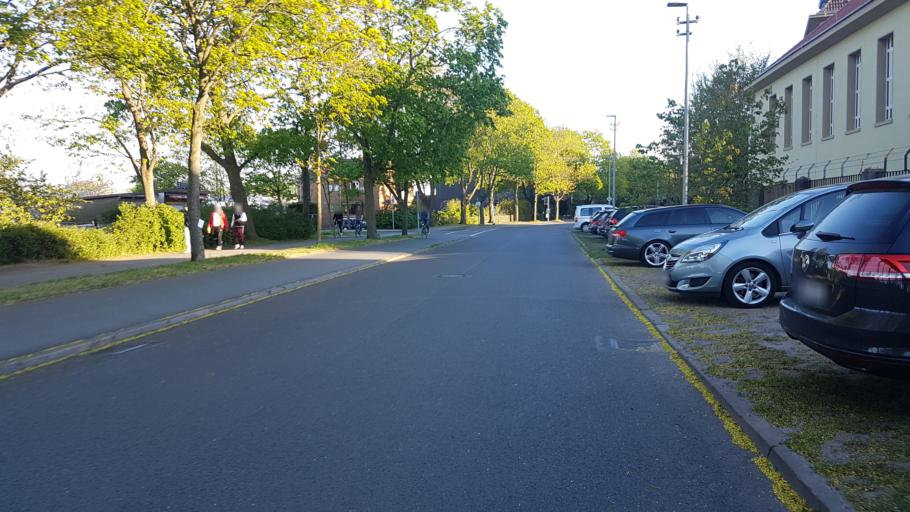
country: DE
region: Lower Saxony
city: Hannover
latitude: 52.4009
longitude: 9.7492
